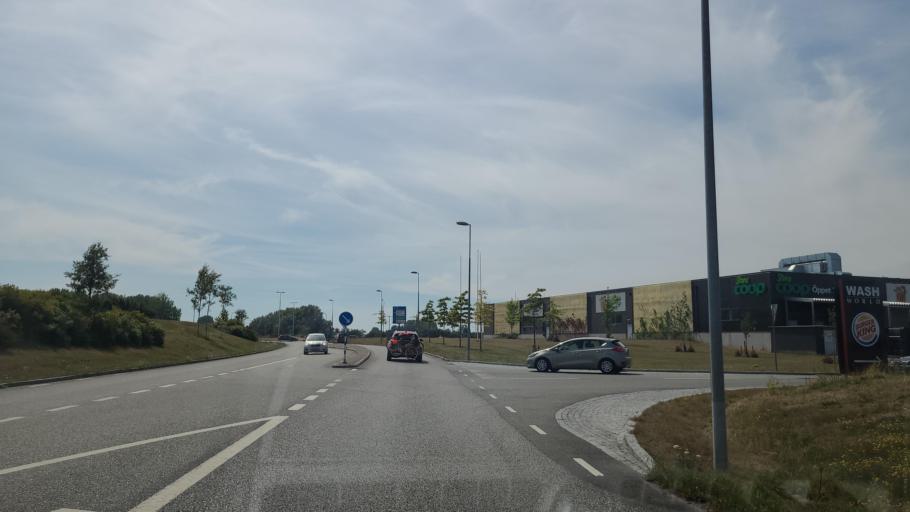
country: SE
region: Skane
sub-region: Trelleborgs Kommun
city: Trelleborg
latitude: 55.3845
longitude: 13.1278
